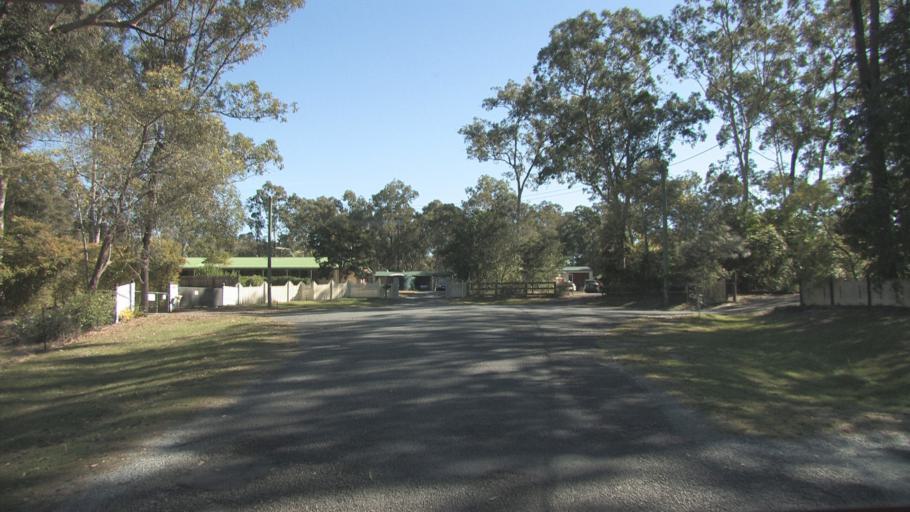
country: AU
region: Queensland
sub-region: Ipswich
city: Springfield Lakes
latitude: -27.7119
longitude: 152.9521
